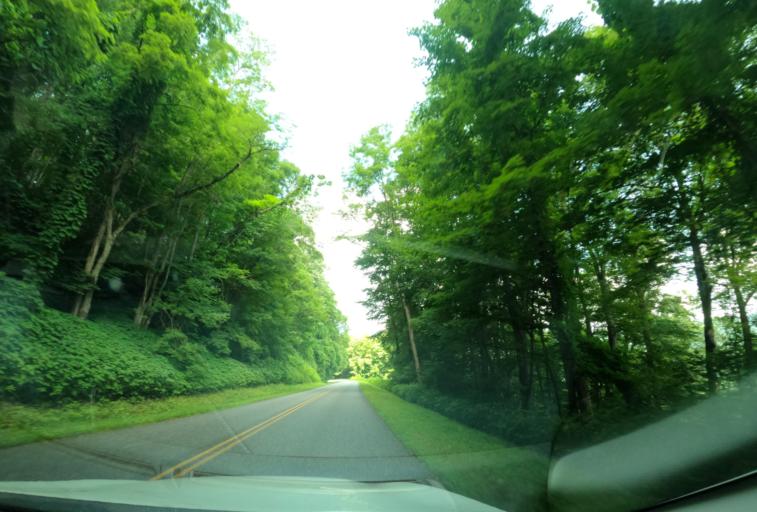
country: US
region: North Carolina
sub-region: Haywood County
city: Hazelwood
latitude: 35.4393
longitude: -83.0513
